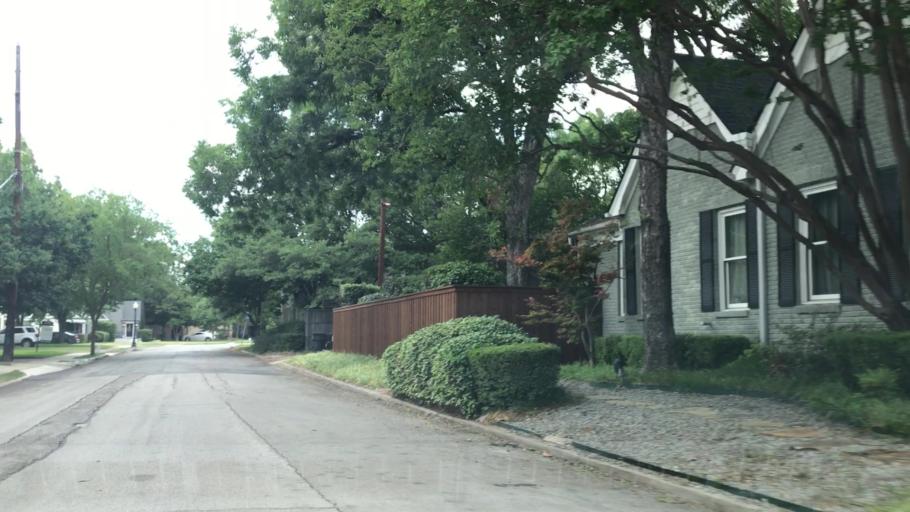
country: US
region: Texas
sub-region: Dallas County
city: Highland Park
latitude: 32.8265
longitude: -96.7823
